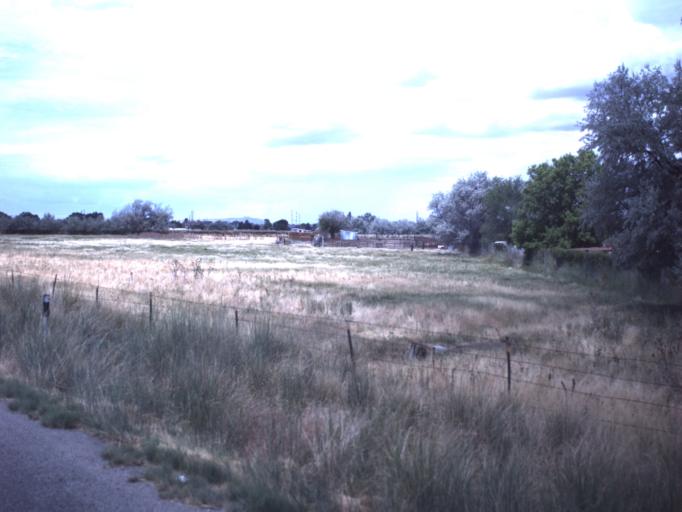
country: US
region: Utah
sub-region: Weber County
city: West Haven
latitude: 41.2034
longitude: -112.0323
